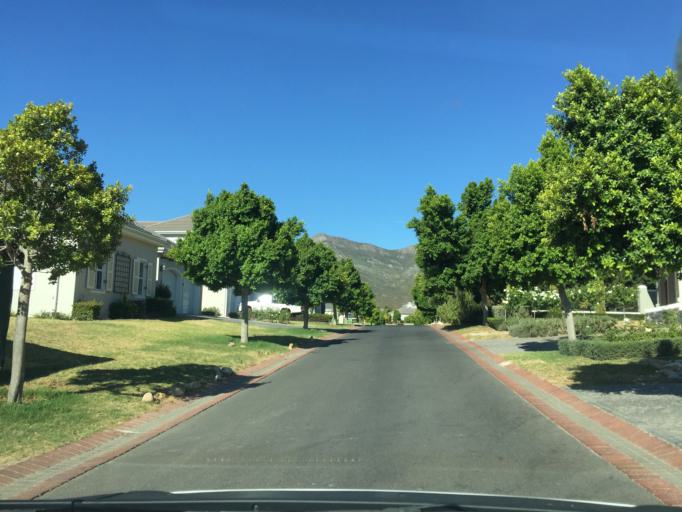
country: ZA
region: Western Cape
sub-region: Cape Winelands District Municipality
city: Paarl
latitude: -33.8049
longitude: 18.9767
